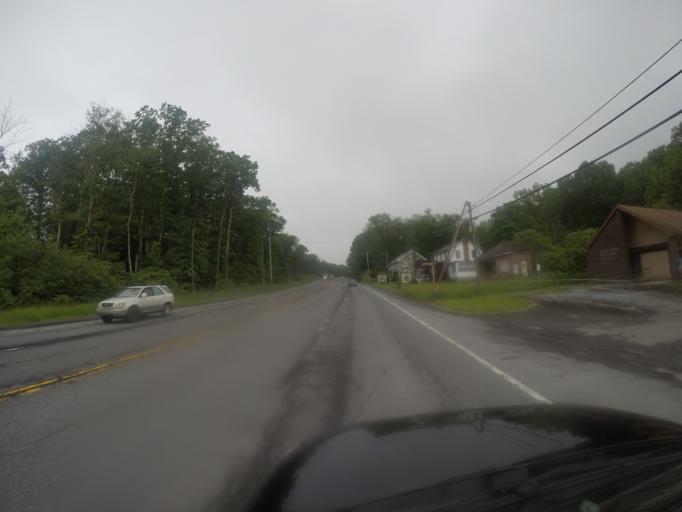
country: US
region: New York
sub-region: Ulster County
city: West Hurley
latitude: 41.9958
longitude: -74.0926
